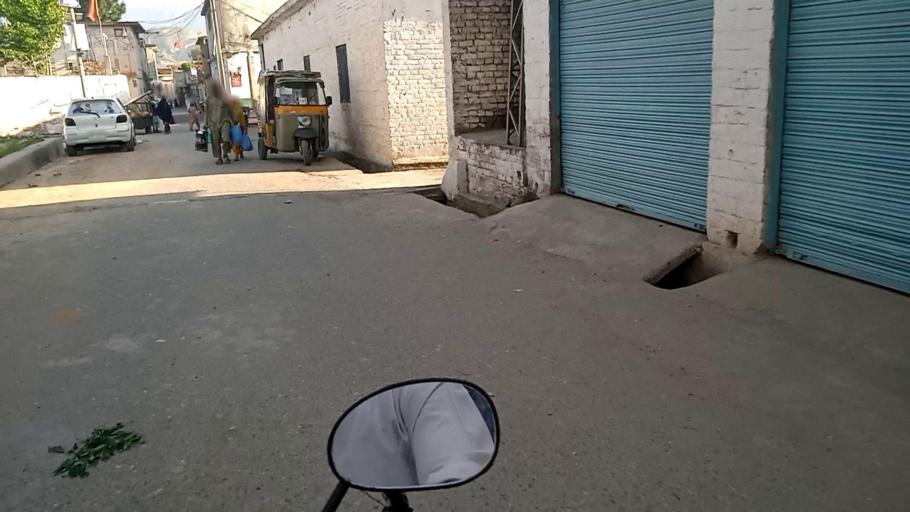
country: PK
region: Khyber Pakhtunkhwa
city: Mingora
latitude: 34.8105
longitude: 72.3606
